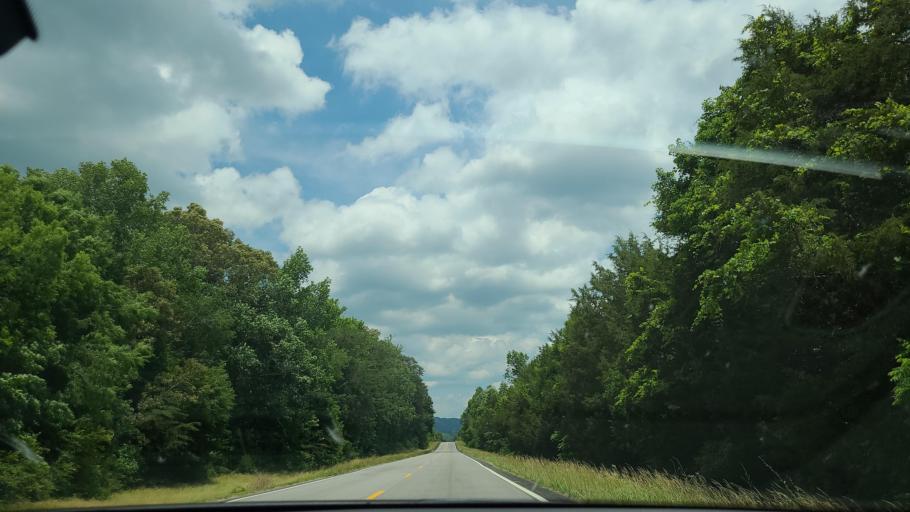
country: US
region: Tennessee
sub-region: Cumberland County
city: Lake Tansi
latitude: 35.7263
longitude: -85.0848
